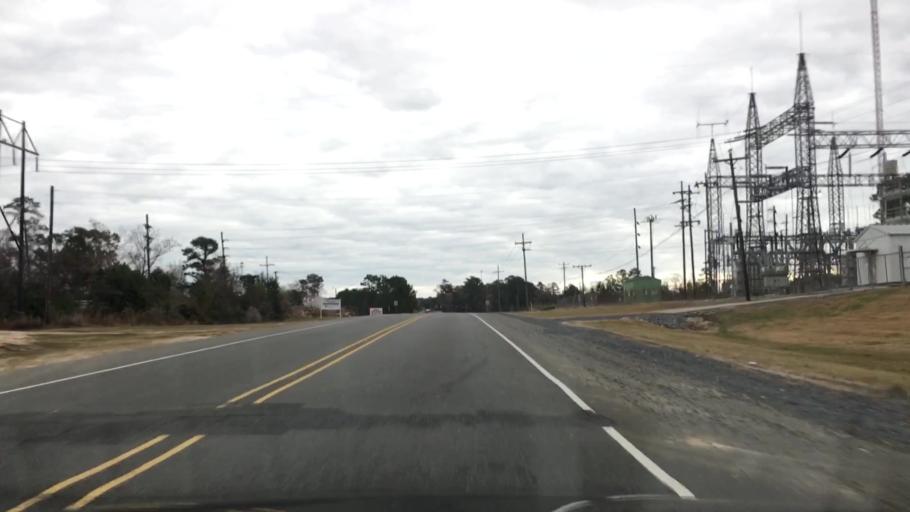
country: US
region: Louisiana
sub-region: Vernon Parish
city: Fort Polk South
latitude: 31.0567
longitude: -93.2535
